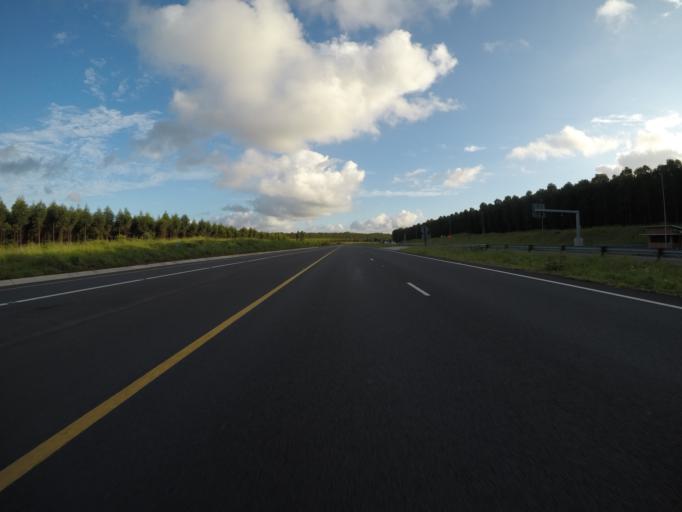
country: ZA
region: KwaZulu-Natal
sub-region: uThungulu District Municipality
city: KwaMbonambi
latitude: -28.5225
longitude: 32.1382
